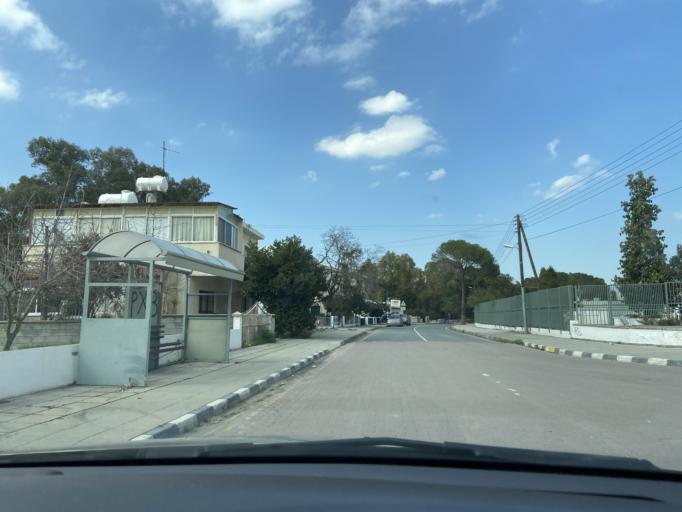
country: CY
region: Lefkosia
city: Alampra
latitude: 35.0156
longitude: 33.3924
